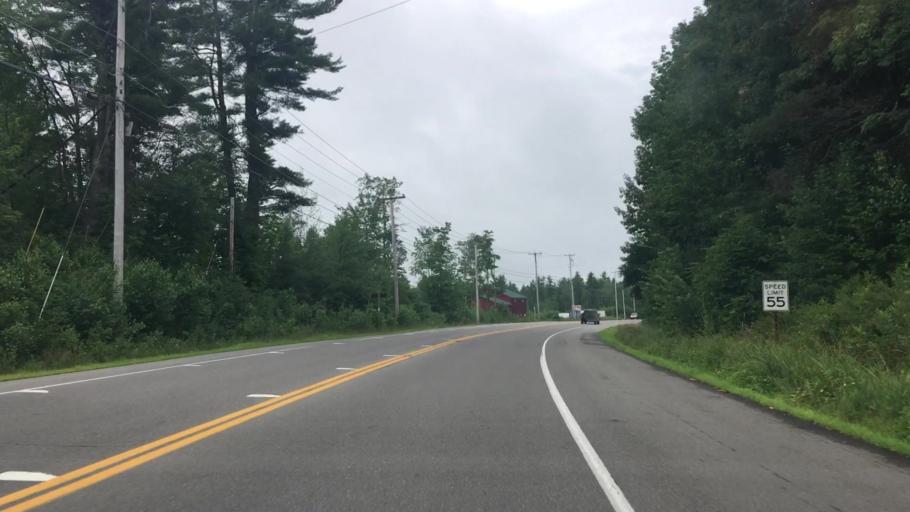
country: US
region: Maine
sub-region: York County
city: Lebanon
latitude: 43.3804
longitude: -70.8778
